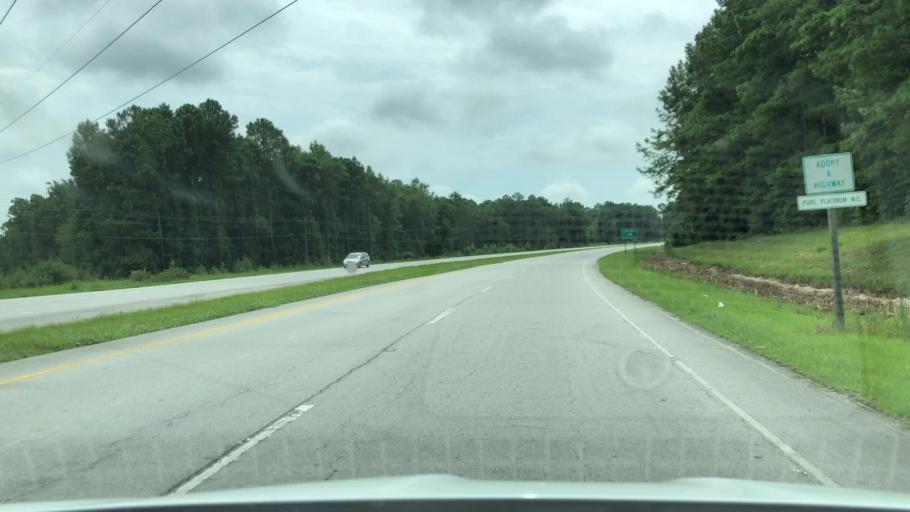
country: US
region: North Carolina
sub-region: Craven County
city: Havelock
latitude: 34.8438
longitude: -76.8828
